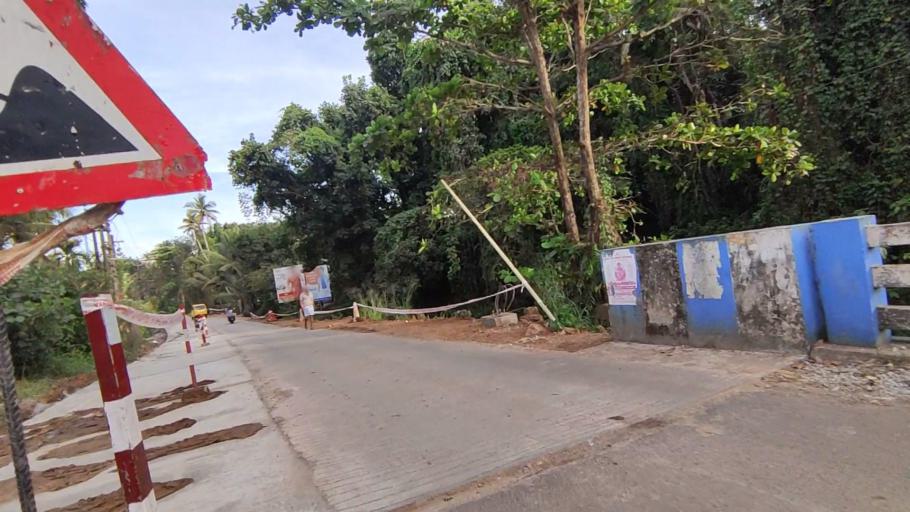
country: IN
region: Kerala
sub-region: Kottayam
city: Kottayam
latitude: 9.6085
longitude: 76.4890
